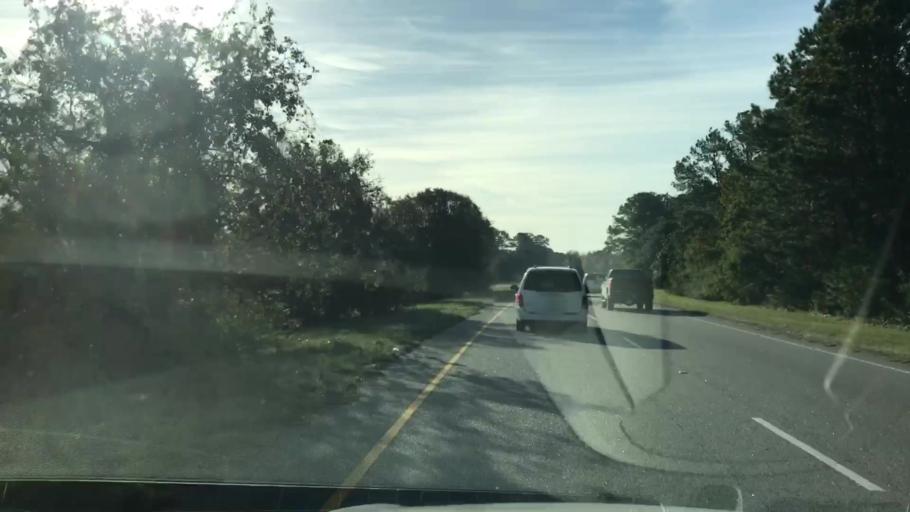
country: US
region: South Carolina
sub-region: Beaufort County
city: Laurel Bay
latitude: 32.5062
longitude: -80.7457
